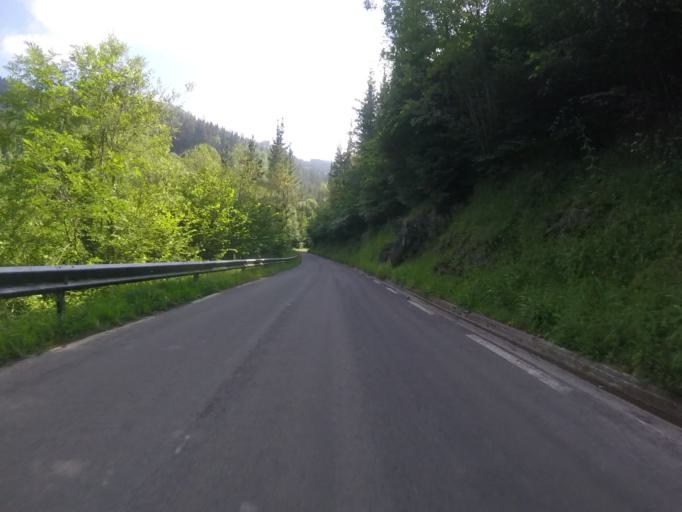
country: ES
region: Basque Country
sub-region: Provincia de Guipuzcoa
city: Beasain
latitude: 43.0798
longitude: -2.2238
